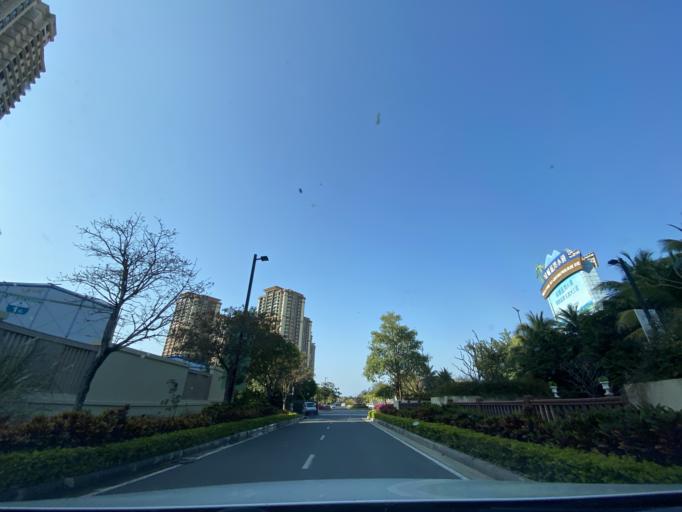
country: CN
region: Hainan
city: Xincun
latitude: 18.4214
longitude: 109.9425
